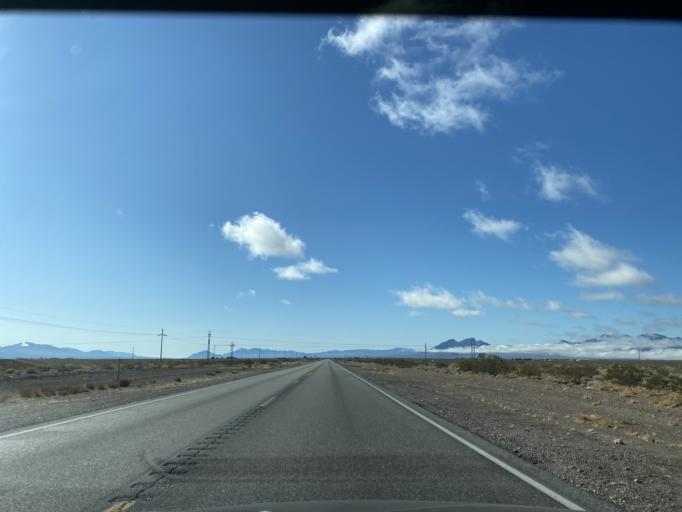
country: US
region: Nevada
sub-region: Nye County
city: Beatty
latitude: 36.5432
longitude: -116.4175
